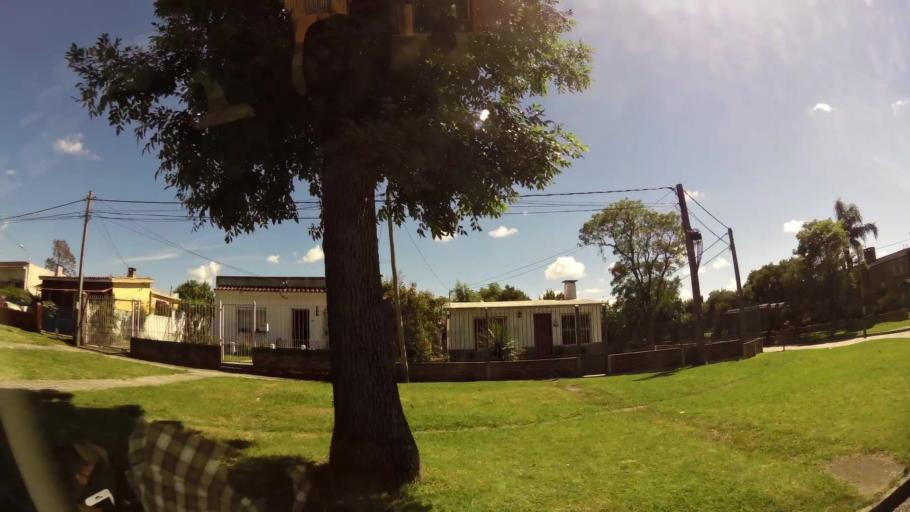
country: UY
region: Canelones
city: Paso de Carrasco
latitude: -34.8444
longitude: -56.1189
